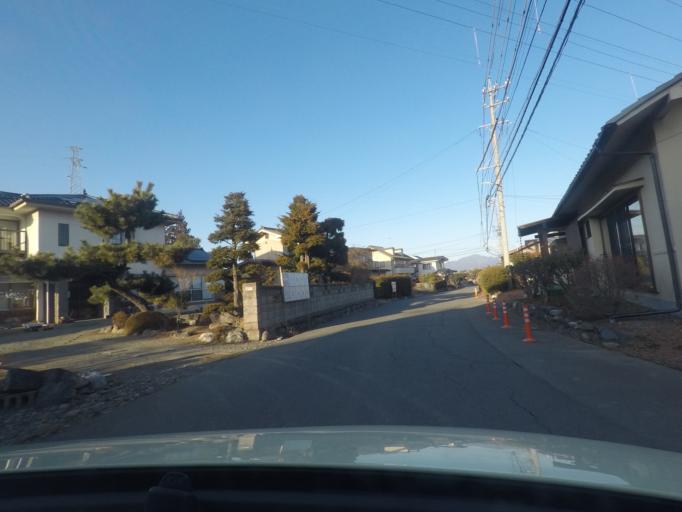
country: JP
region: Nagano
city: Matsumoto
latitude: 36.2105
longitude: 137.8849
